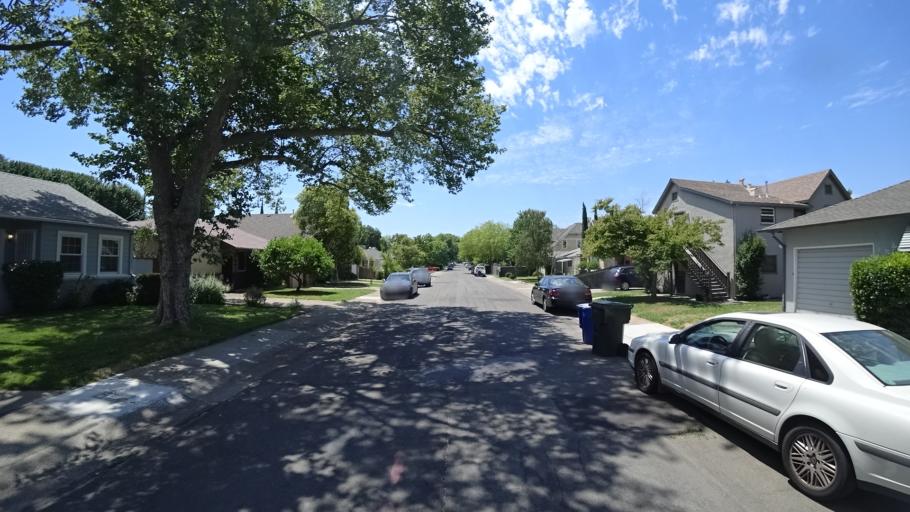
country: US
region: California
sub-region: Sacramento County
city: Sacramento
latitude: 38.5703
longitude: -121.4352
